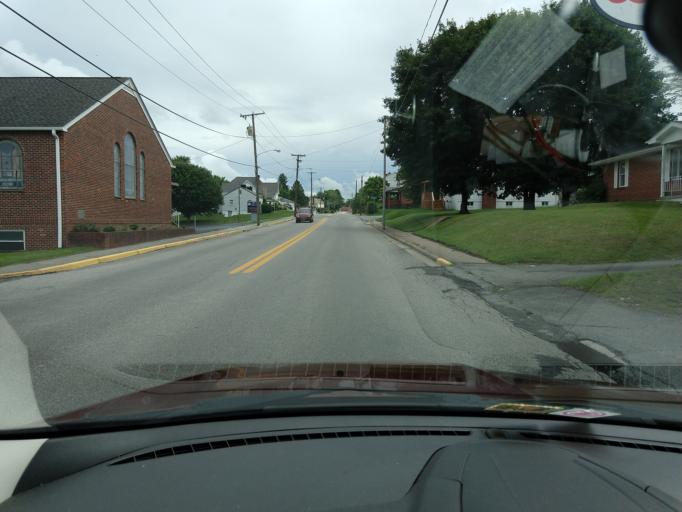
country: US
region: West Virginia
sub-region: Fayette County
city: Oak Hill
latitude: 37.9745
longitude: -81.1542
